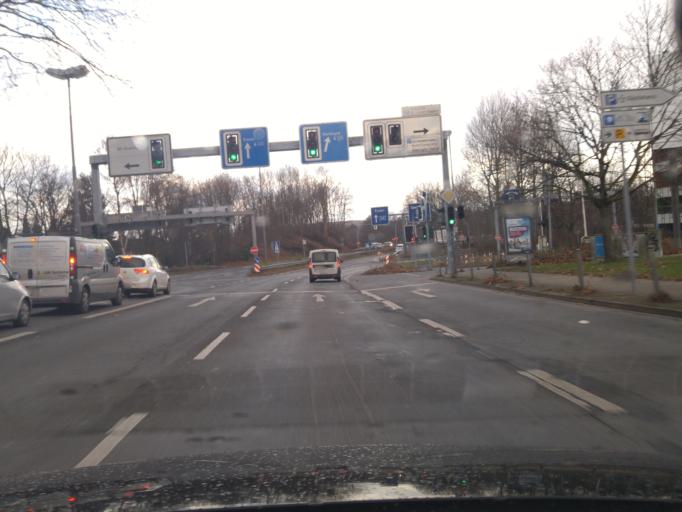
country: DE
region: North Rhine-Westphalia
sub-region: Regierungsbezirk Arnsberg
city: Bochum
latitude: 51.4928
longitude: 7.2324
